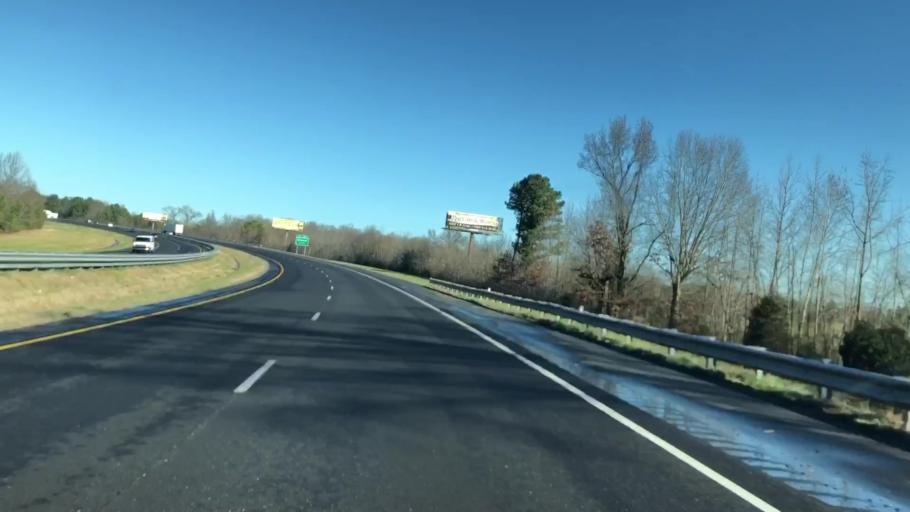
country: US
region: Alabama
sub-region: Limestone County
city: Ardmore
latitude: 34.9010
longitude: -86.9062
